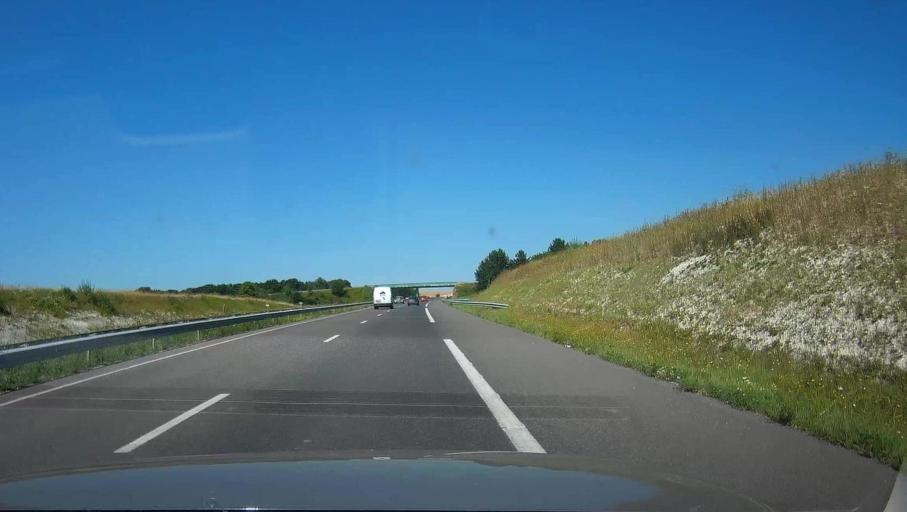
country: FR
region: Champagne-Ardenne
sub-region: Departement de la Marne
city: Fagnieres
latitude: 49.0293
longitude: 4.2849
